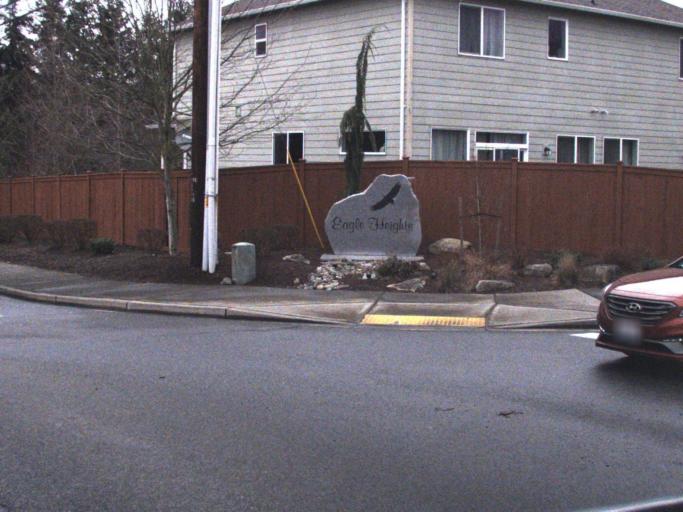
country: US
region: Washington
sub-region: Snohomish County
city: Sisco Heights
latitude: 48.1517
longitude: -122.1165
